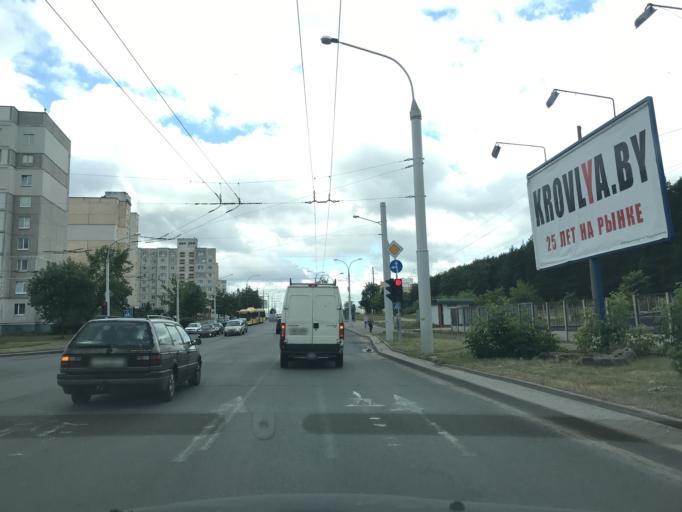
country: BY
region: Minsk
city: Borovlyany
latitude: 53.9545
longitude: 27.6891
